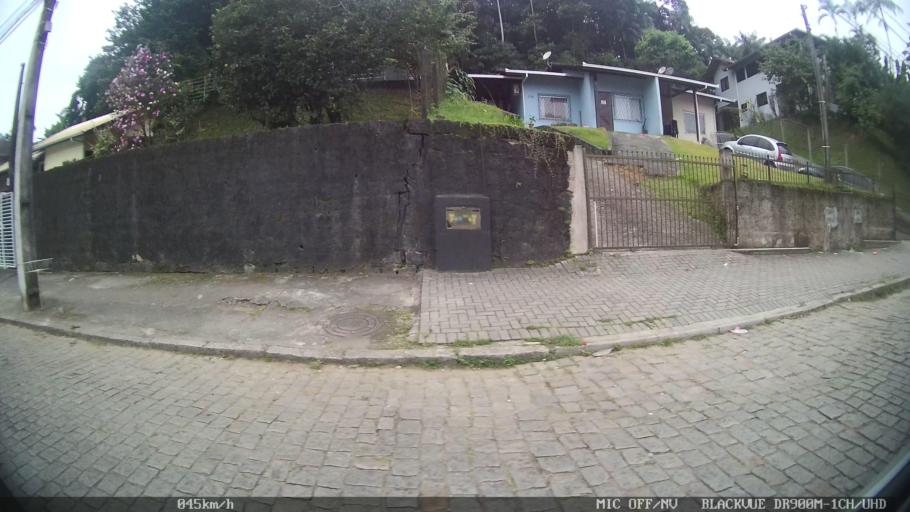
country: BR
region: Santa Catarina
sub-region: Joinville
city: Joinville
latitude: -26.3386
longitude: -48.8574
